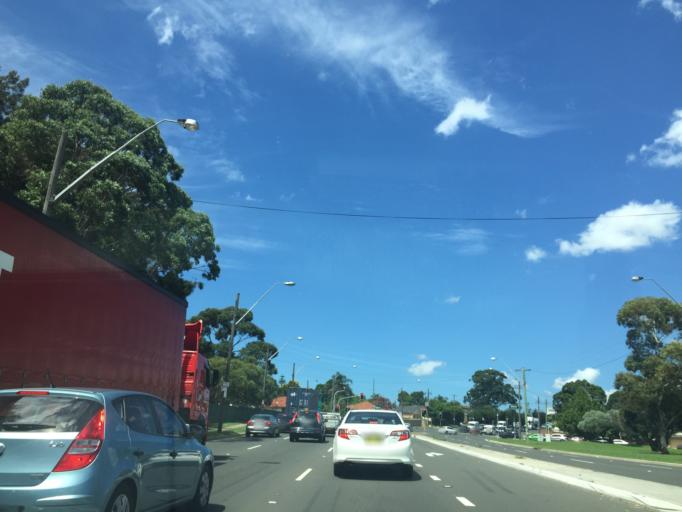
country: AU
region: New South Wales
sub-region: Canterbury
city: Lakemba
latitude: -33.9066
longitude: 151.0641
